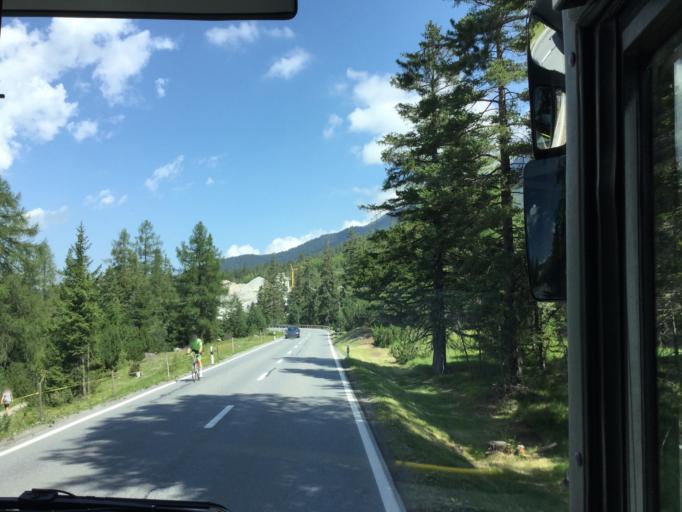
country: CH
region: Grisons
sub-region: Albula District
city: Tiefencastel
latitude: 46.7044
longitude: 9.5600
